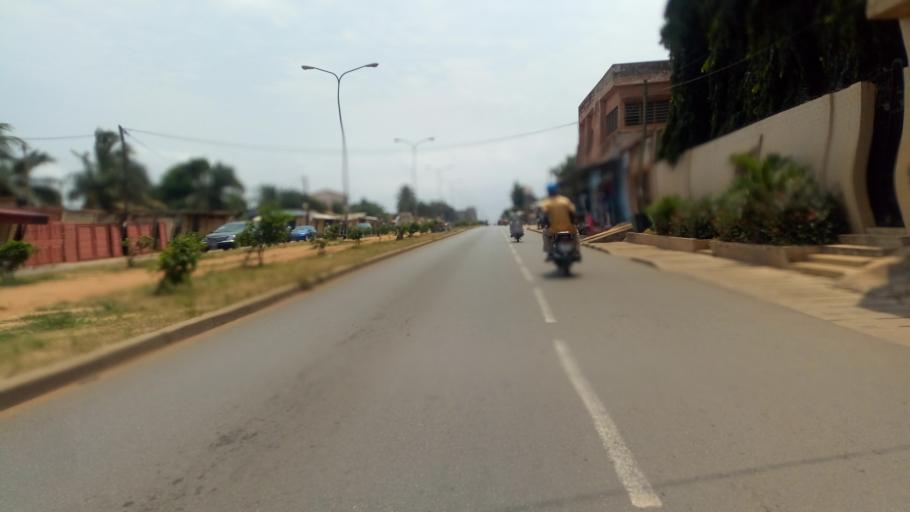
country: TG
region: Maritime
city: Lome
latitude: 6.1902
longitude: 1.2510
